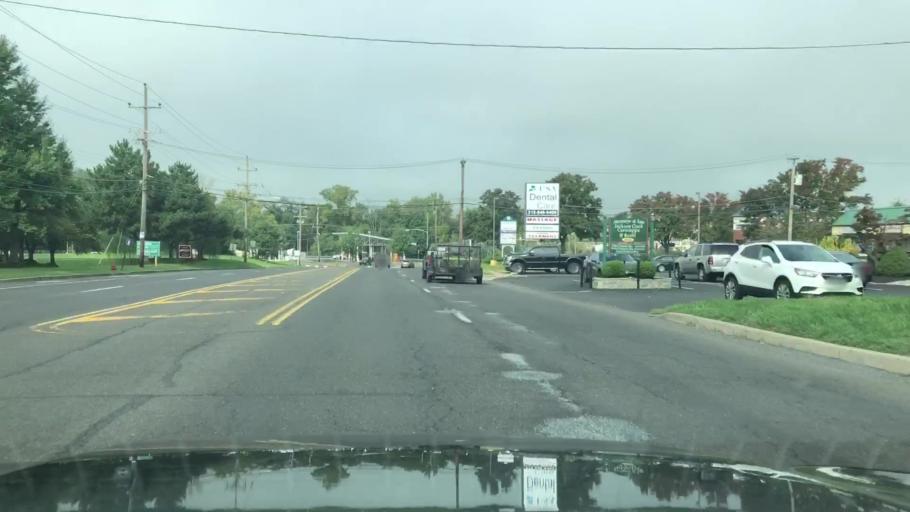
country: US
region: Pennsylvania
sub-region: Bucks County
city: Fairless Hills
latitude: 40.1788
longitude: -74.8681
